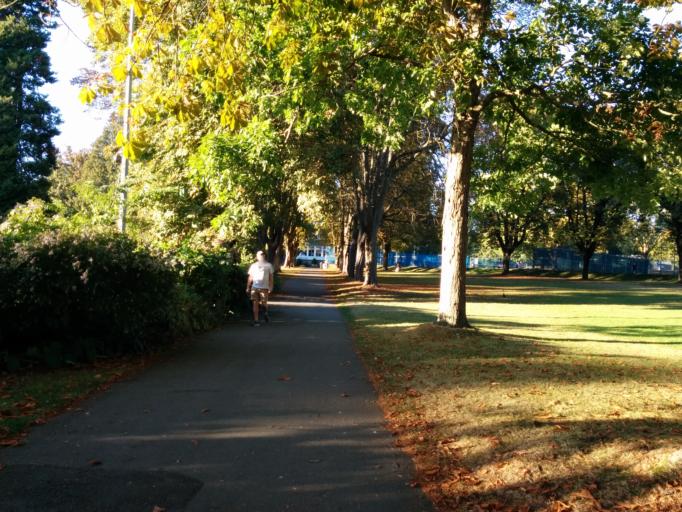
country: CA
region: British Columbia
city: West End
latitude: 49.2911
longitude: -123.1466
